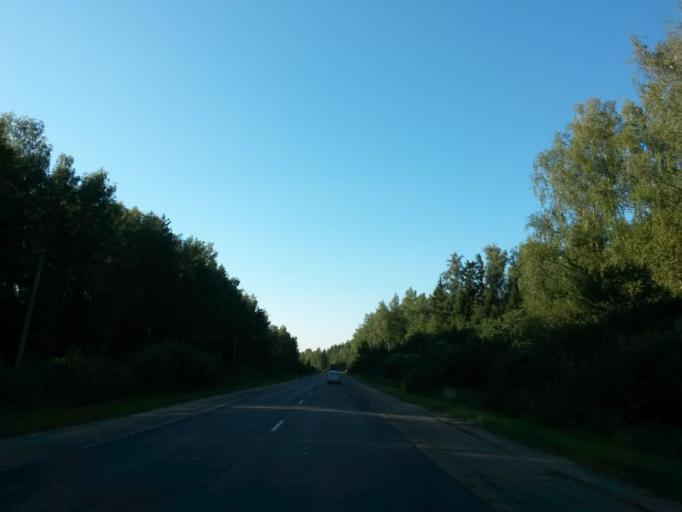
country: RU
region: Ivanovo
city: Novo-Talitsy
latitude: 57.0490
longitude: 40.7371
